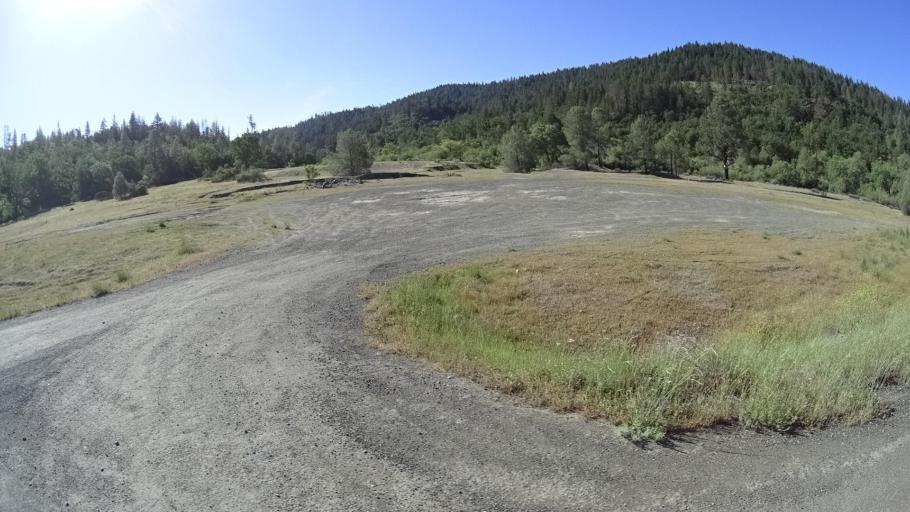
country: US
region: California
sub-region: Lake County
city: Upper Lake
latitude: 39.4120
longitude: -122.9760
